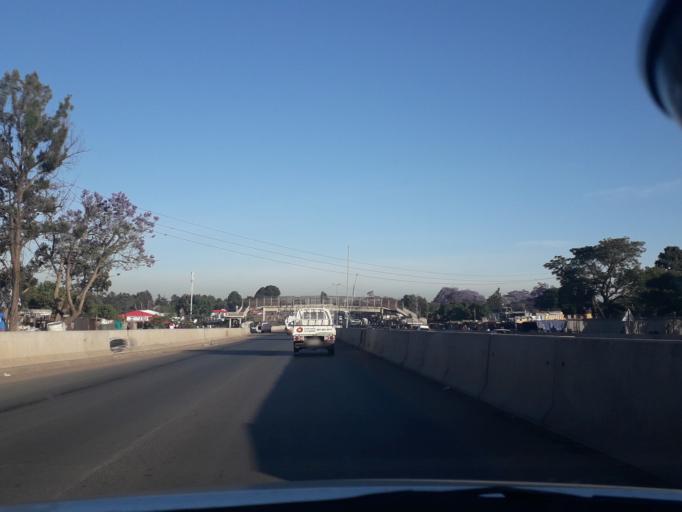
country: ZA
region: Gauteng
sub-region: West Rand District Municipality
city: Muldersdriseloop
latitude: -26.0641
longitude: 27.9051
